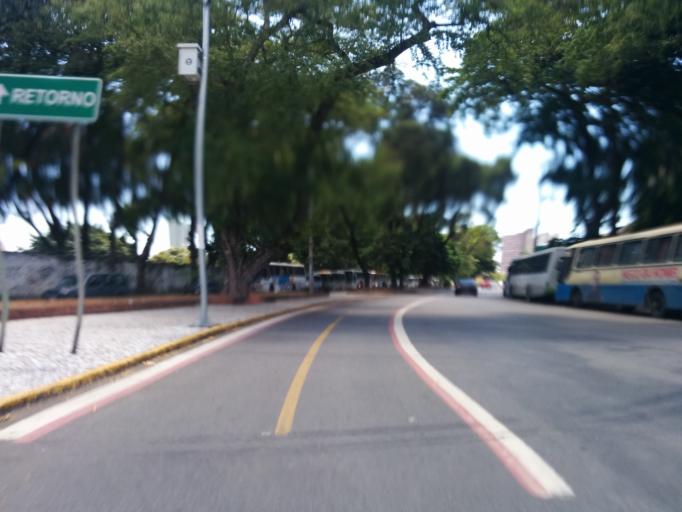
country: BR
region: Pernambuco
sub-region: Recife
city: Recife
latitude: -8.0499
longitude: -34.8876
